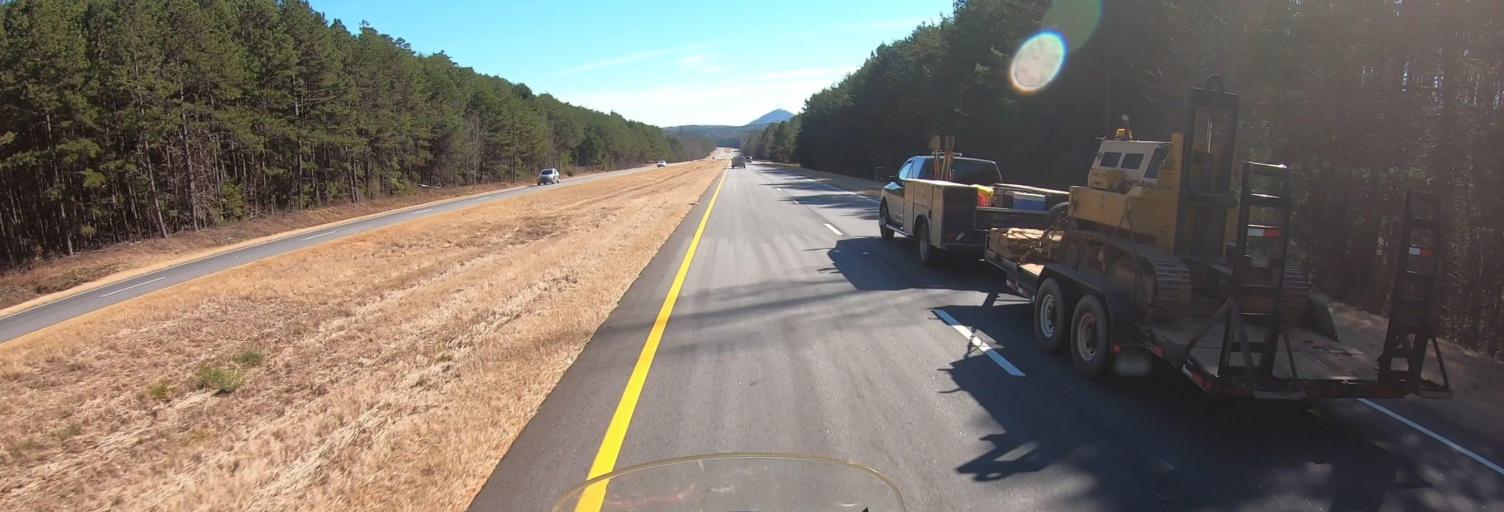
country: US
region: Georgia
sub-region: Stephens County
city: Toccoa
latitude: 34.5780
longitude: -83.4069
